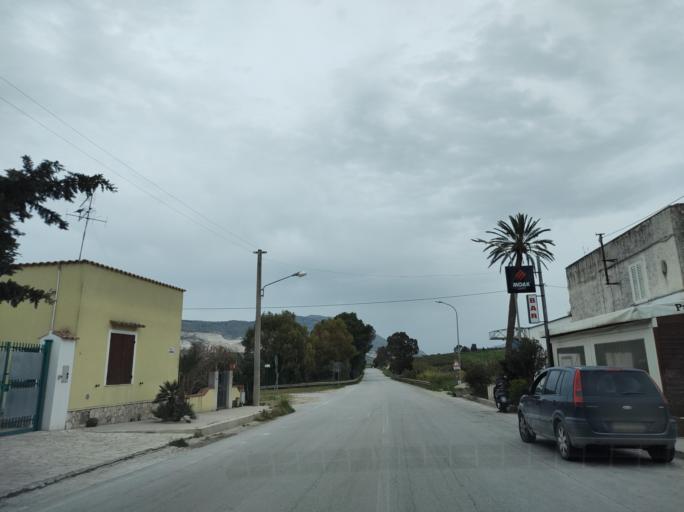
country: IT
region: Sicily
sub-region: Trapani
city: Custonaci
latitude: 38.0413
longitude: 12.6736
